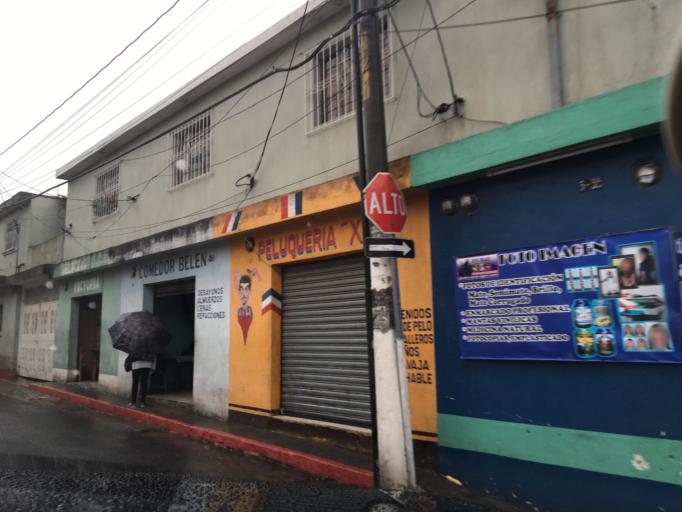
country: GT
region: Guatemala
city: Santa Catarina Pinula
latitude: 14.5707
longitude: -90.4971
